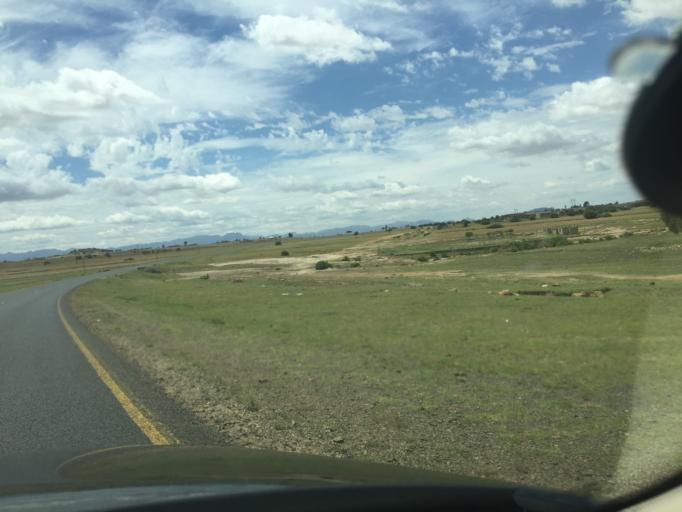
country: LS
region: Mafeteng
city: Mafeteng
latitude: -29.9717
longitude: 27.3130
